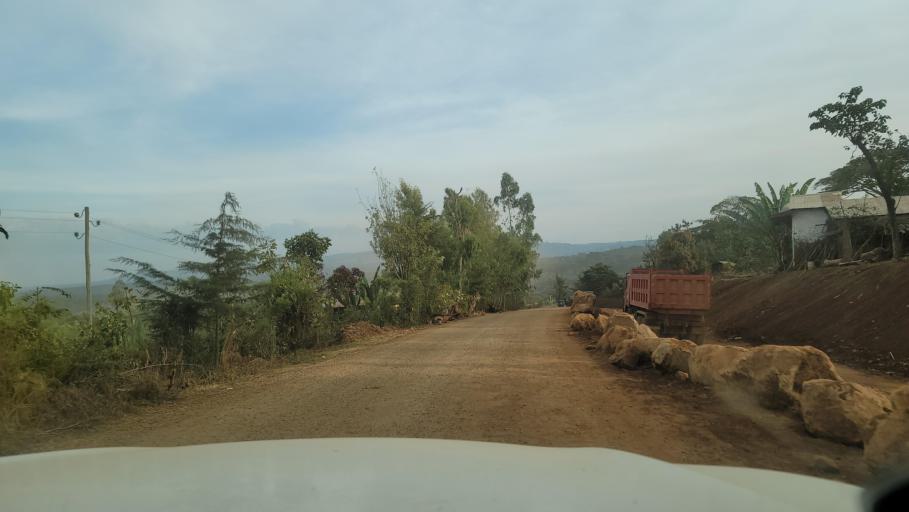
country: ET
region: Oromiya
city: Agaro
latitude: 7.8241
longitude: 36.5331
